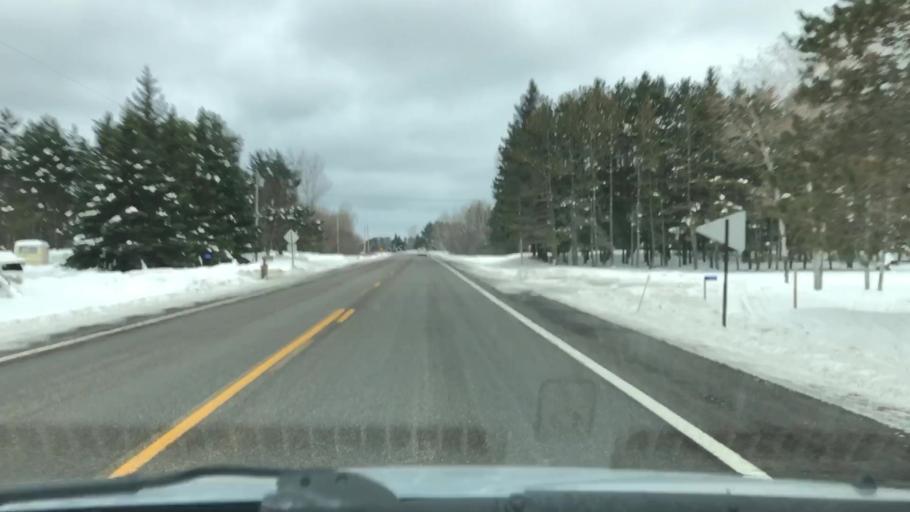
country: US
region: Minnesota
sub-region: Carlton County
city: Esko
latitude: 46.6831
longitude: -92.3672
